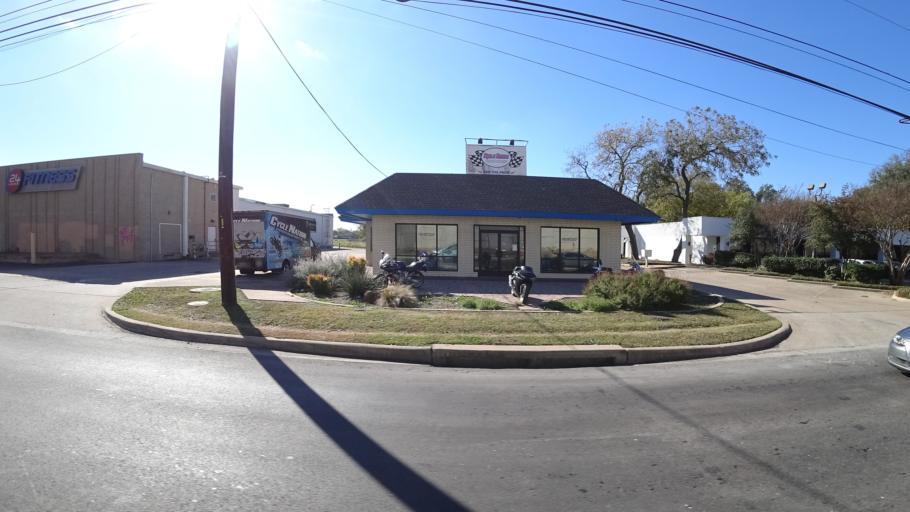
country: US
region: Texas
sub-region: Williamson County
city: Anderson Mill
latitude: 30.4639
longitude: -97.7957
